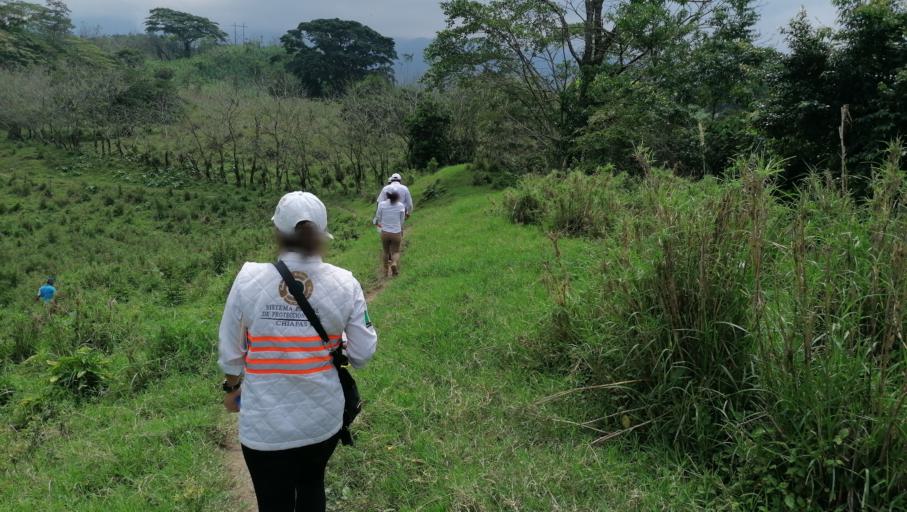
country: MX
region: Chiapas
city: Ocotepec
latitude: 17.2943
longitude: -93.2267
